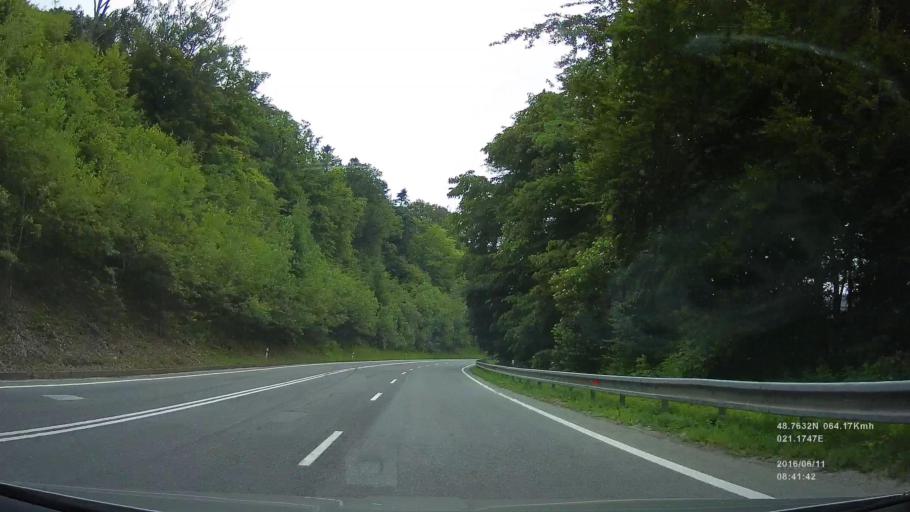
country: SK
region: Kosicky
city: Kosice
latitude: 48.7602
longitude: 21.1795
